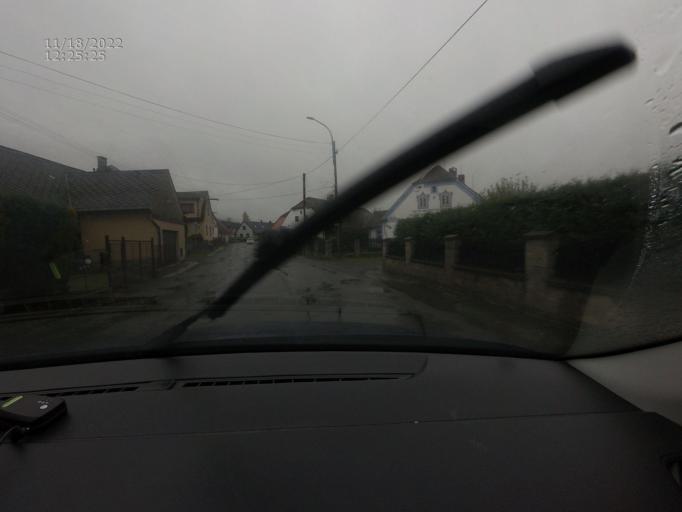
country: CZ
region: Plzensky
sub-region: Okres Klatovy
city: Planice
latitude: 49.4407
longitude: 13.5150
